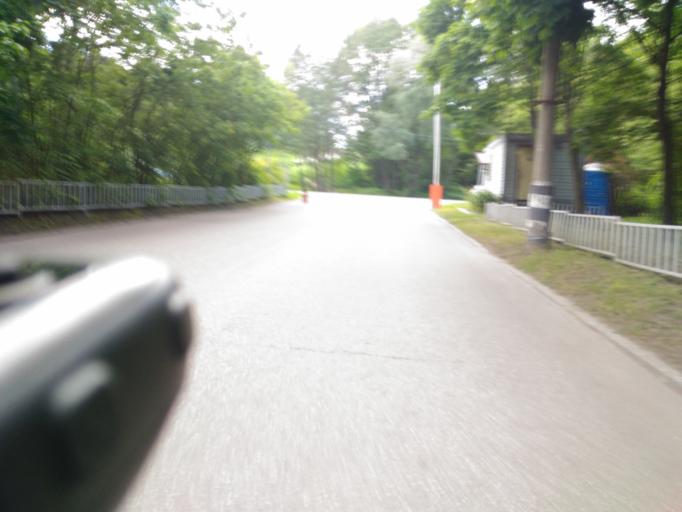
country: RU
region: Moscow
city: Shchukino
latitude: 55.7649
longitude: 37.4306
